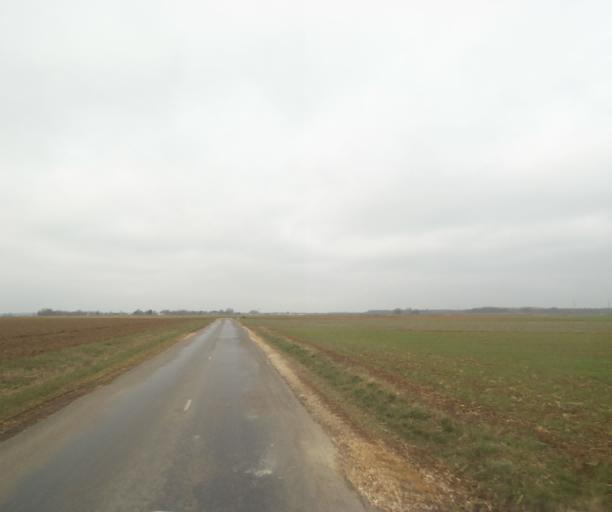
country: FR
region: Champagne-Ardenne
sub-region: Departement de la Haute-Marne
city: Villiers-en-Lieu
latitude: 48.6779
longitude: 4.8537
